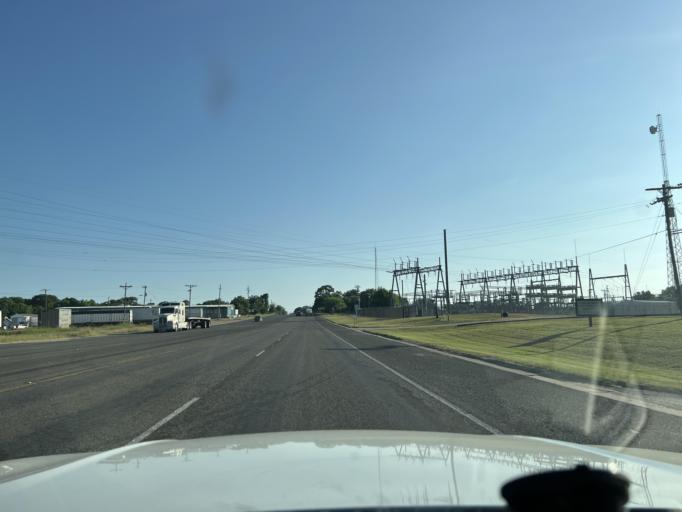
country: US
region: Texas
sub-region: Washington County
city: Brenham
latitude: 30.1823
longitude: -96.3803
